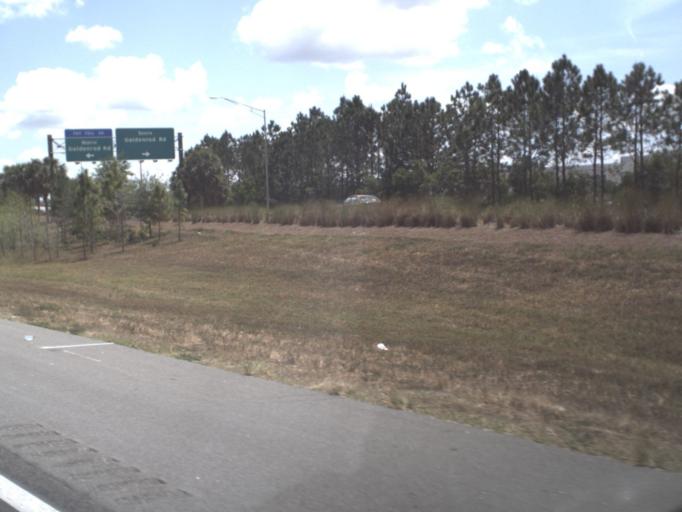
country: US
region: Florida
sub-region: Orange County
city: Conway
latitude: 28.4499
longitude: -81.2913
